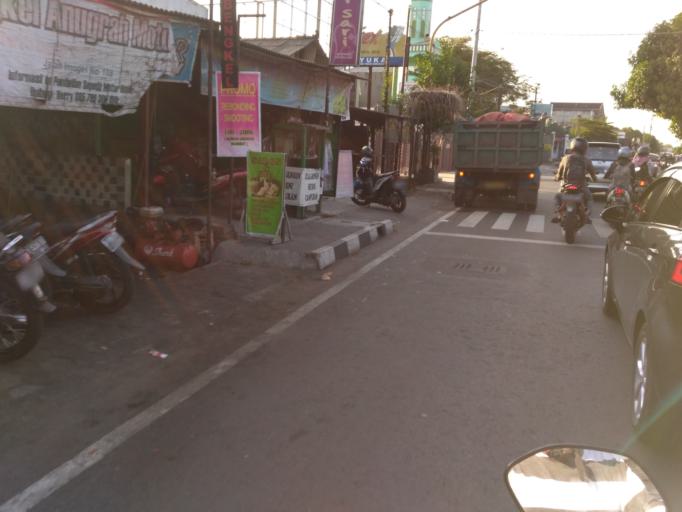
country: ID
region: Daerah Istimewa Yogyakarta
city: Yogyakarta
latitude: -7.8298
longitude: 110.3899
